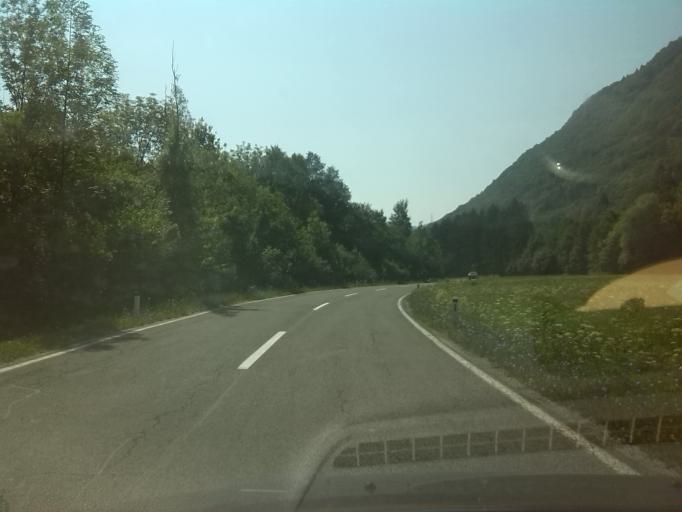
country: SI
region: Tolmin
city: Tolmin
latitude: 46.1954
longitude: 13.6941
